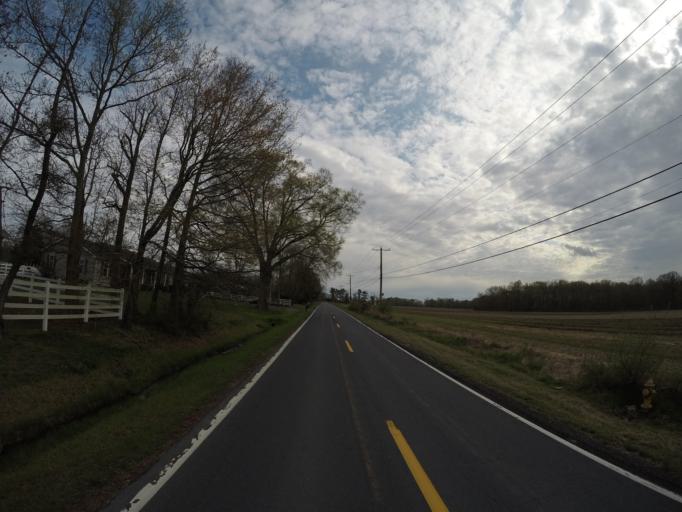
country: US
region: Delaware
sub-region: New Castle County
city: Glasgow
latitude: 39.5686
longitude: -75.7636
